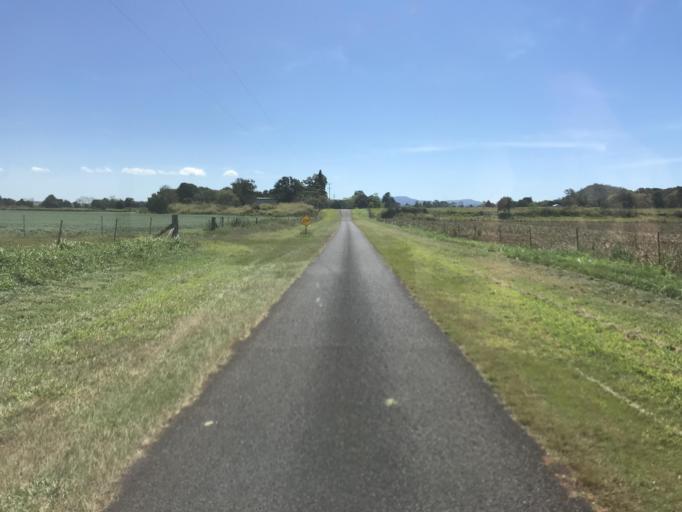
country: AU
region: Queensland
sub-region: Tablelands
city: Atherton
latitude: -17.2819
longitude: 145.5441
